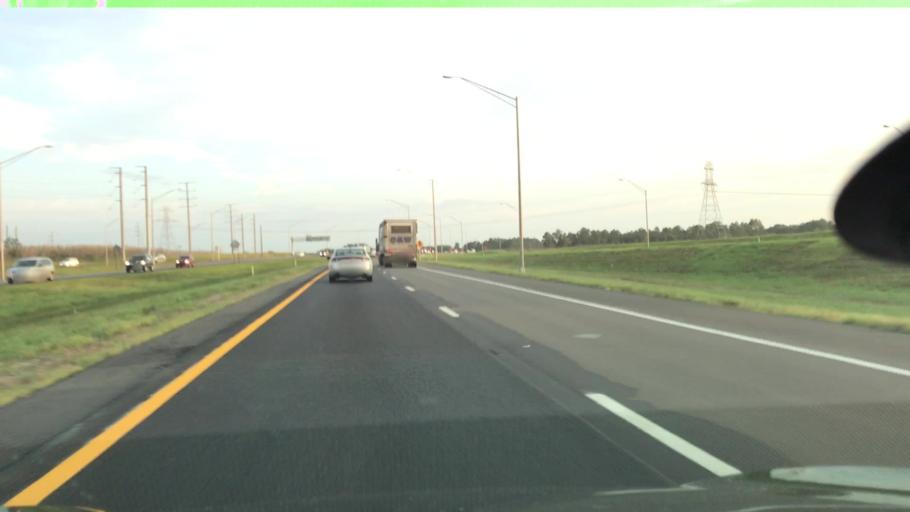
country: US
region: Florida
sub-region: Orange County
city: Oakland
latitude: 28.4763
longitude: -81.6315
